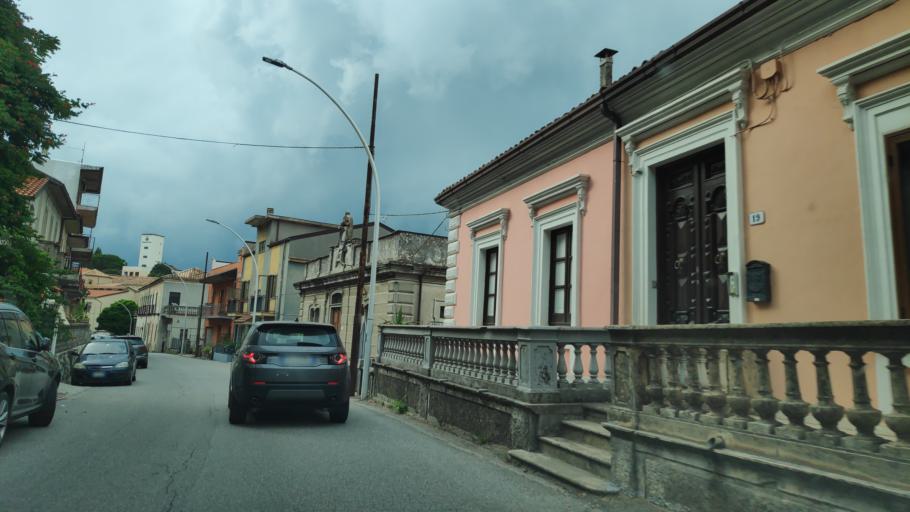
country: IT
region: Calabria
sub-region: Provincia di Catanzaro
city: Chiaravalle Centrale
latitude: 38.6827
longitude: 16.4170
